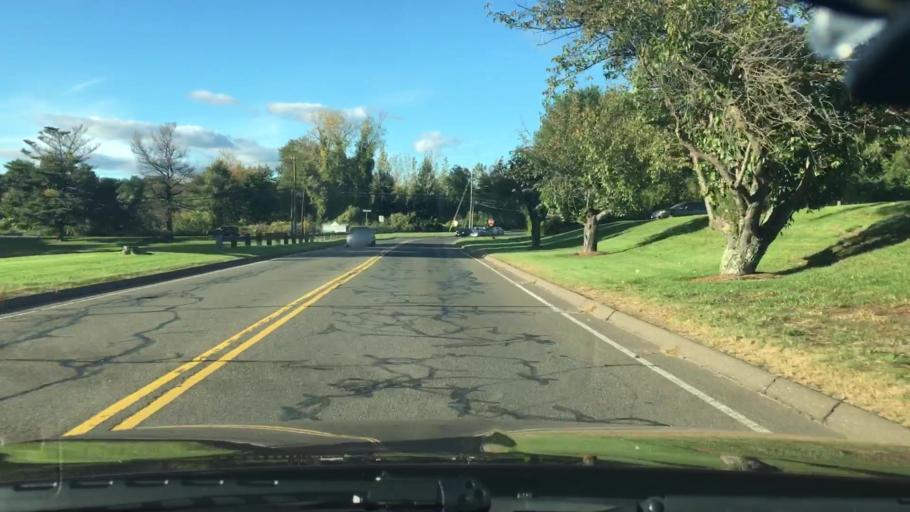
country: US
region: Connecticut
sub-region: Hartford County
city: Windsor
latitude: 41.8641
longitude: -72.6777
